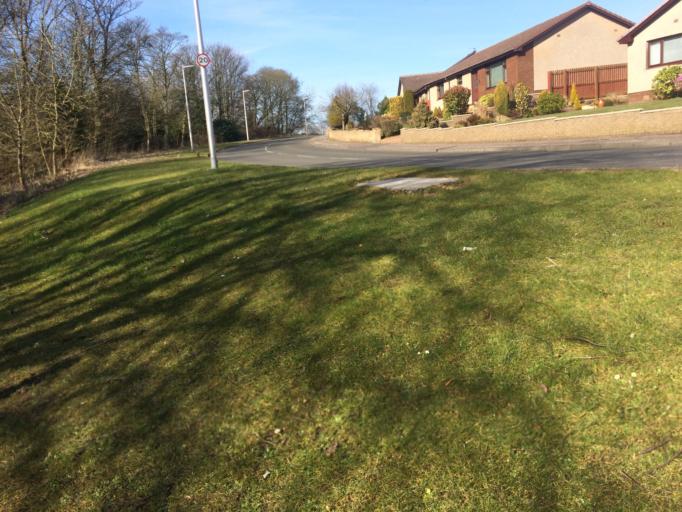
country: GB
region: Scotland
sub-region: Fife
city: Kirkcaldy
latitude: 56.1240
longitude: -3.2068
